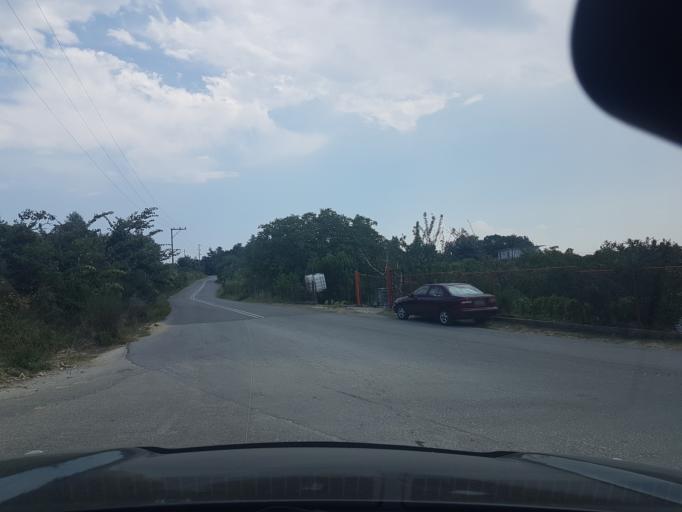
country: GR
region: Central Greece
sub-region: Nomos Evvoias
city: Kymi
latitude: 38.6360
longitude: 24.0689
